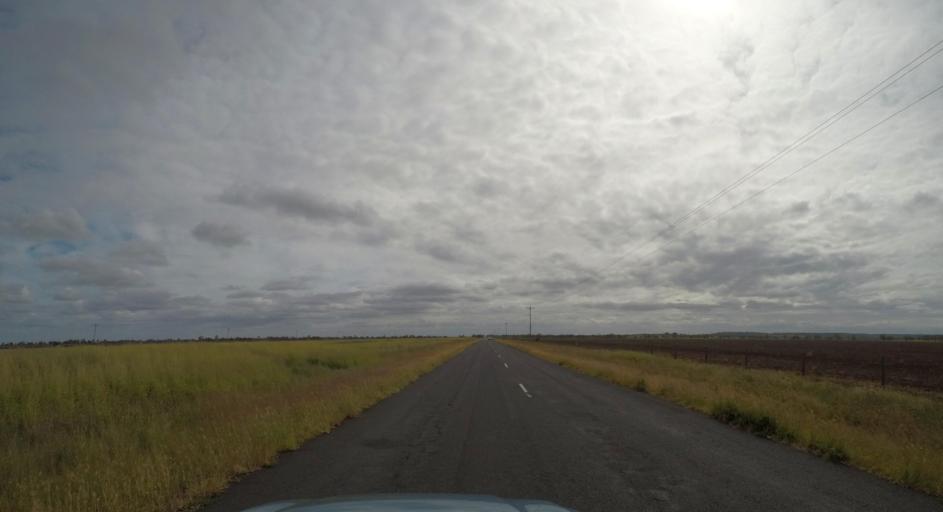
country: AU
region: Queensland
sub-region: Western Downs
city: Dalby
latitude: -26.9987
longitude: 151.2322
